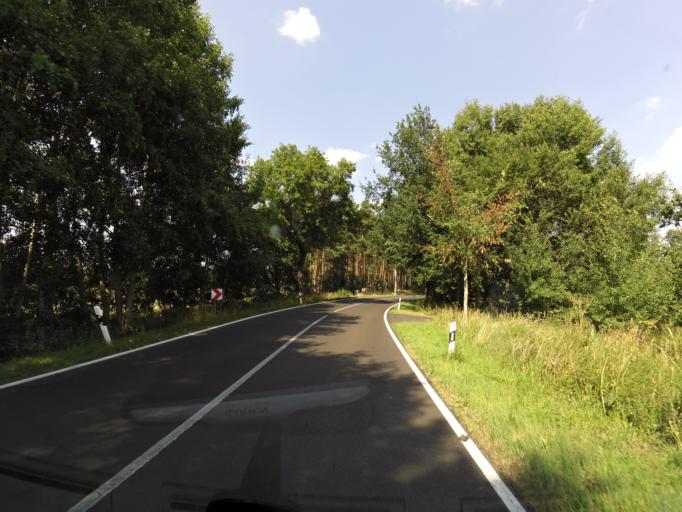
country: DE
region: Brandenburg
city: Liebenwalde
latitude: 52.9261
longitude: 13.3871
